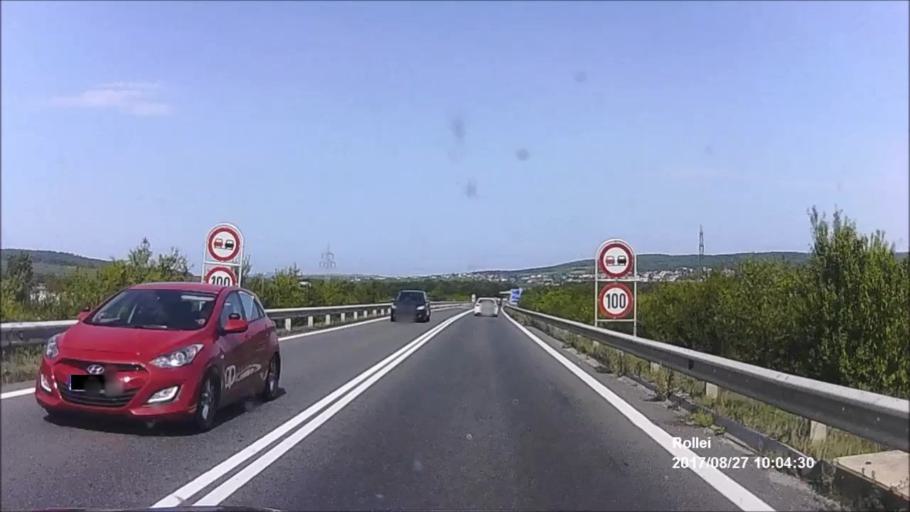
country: AT
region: Burgenland
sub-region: Eisenstadt-Umgebung
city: Wulkaprodersdorf
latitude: 47.8069
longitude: 16.5043
